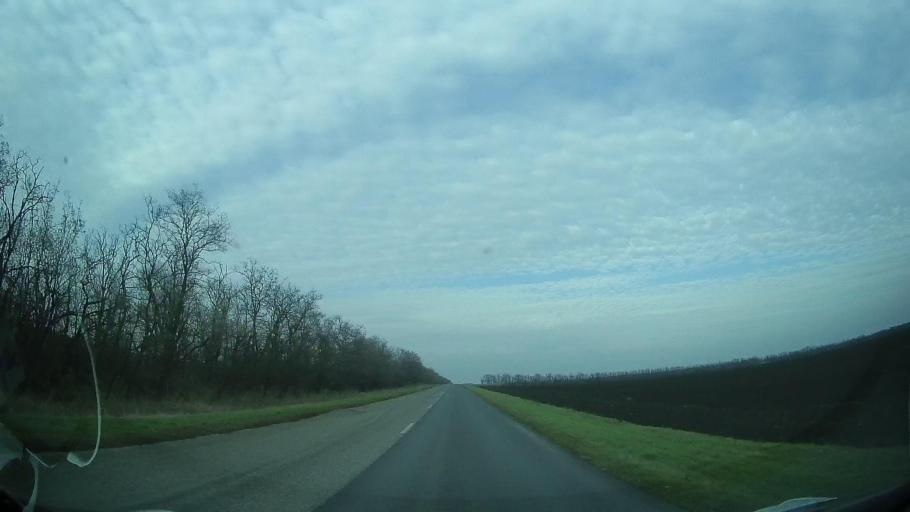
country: RU
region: Rostov
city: Zernograd
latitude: 46.9349
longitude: 40.3665
